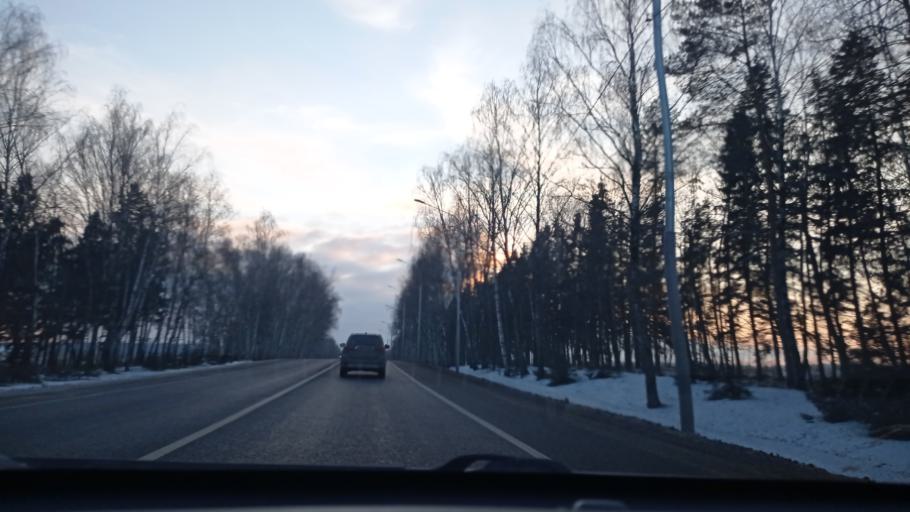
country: RU
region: Moskovskaya
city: Troitsk
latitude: 55.2940
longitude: 37.1316
